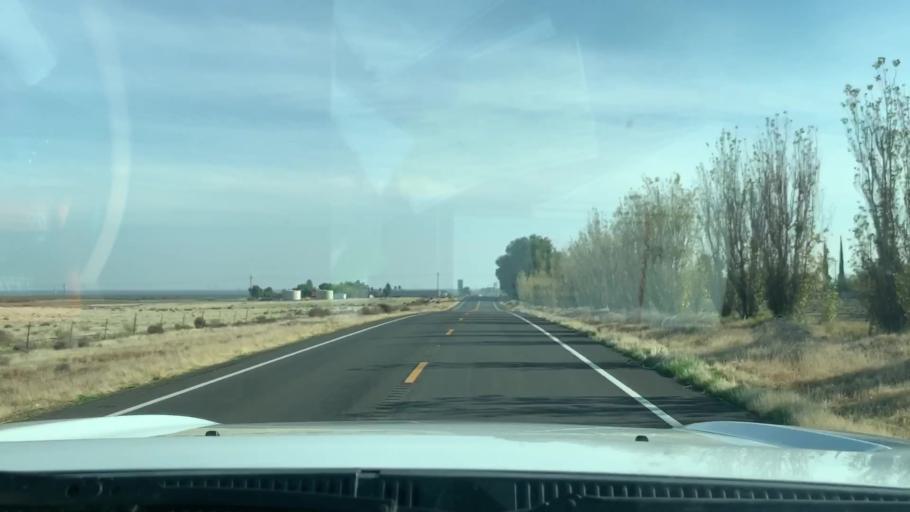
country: US
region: California
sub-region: Fresno County
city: Coalinga
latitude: 36.2542
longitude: -120.2596
